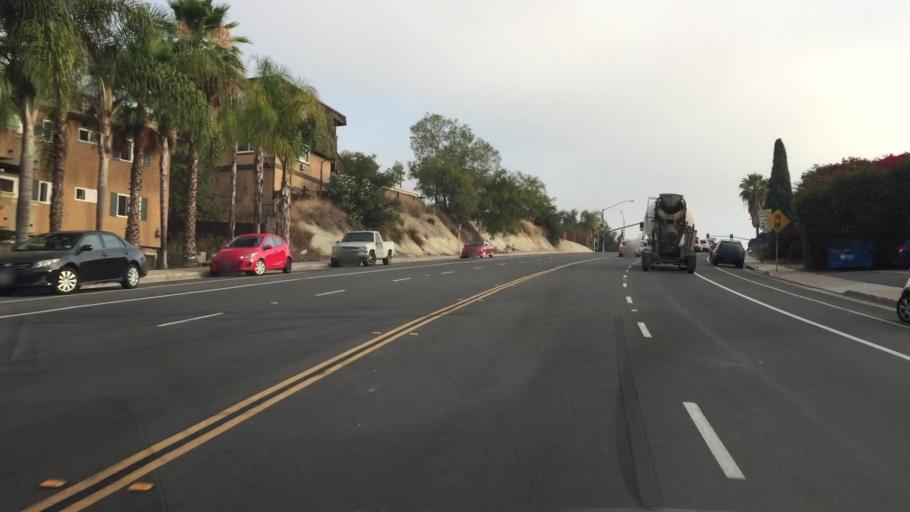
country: US
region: California
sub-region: San Diego County
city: Lemon Grove
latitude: 32.7562
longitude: -117.0661
